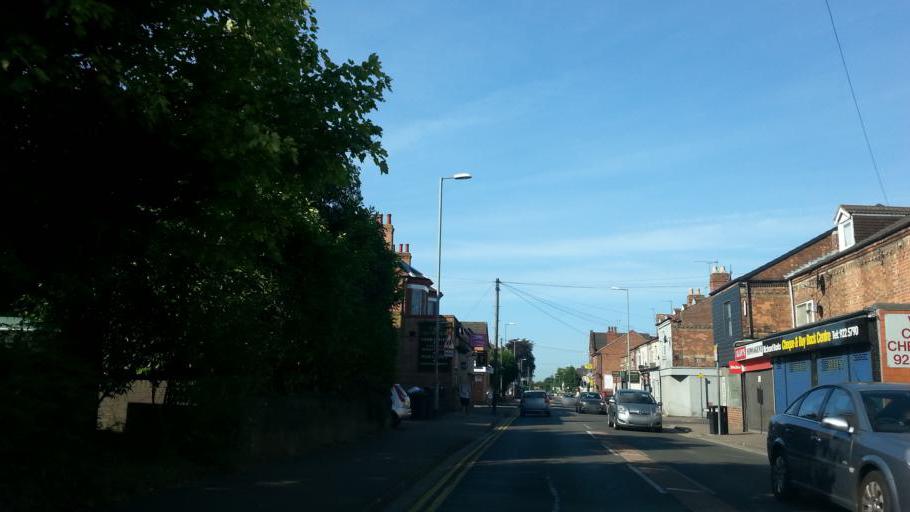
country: GB
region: England
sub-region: Nottinghamshire
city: Gotham
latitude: 52.9258
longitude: -1.2054
